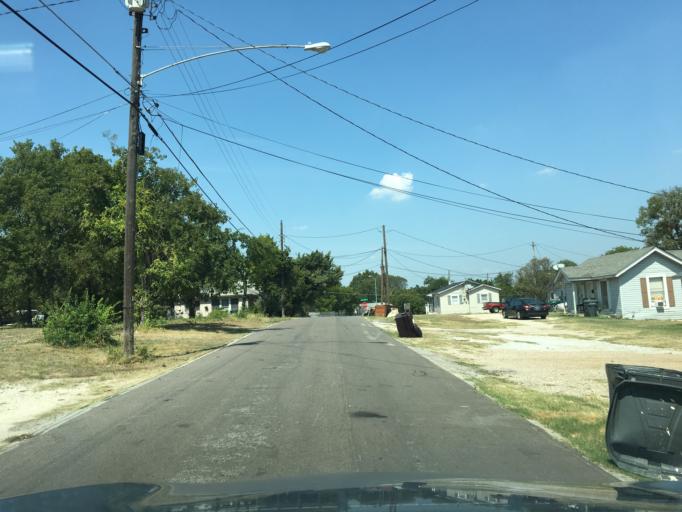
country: US
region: Texas
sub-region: Dallas County
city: Dallas
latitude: 32.7344
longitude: -96.7910
